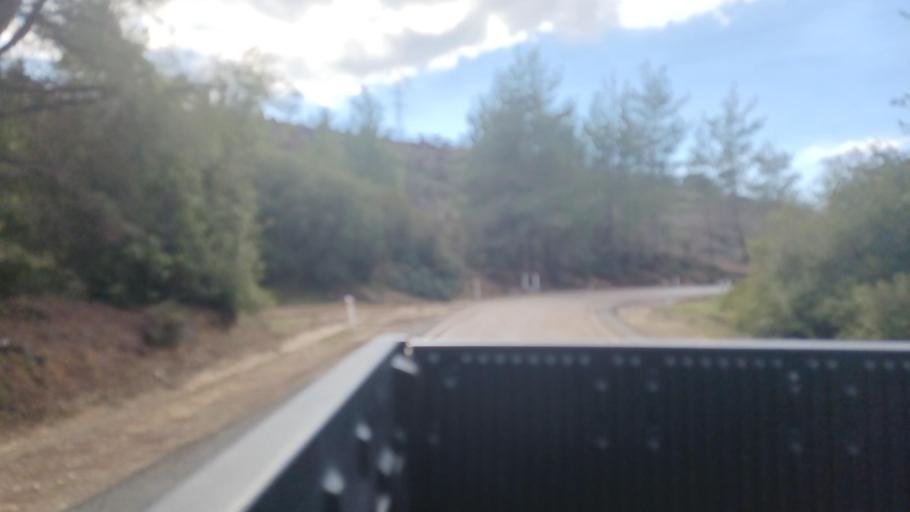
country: CY
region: Limassol
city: Pissouri
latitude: 34.7346
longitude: 32.6449
